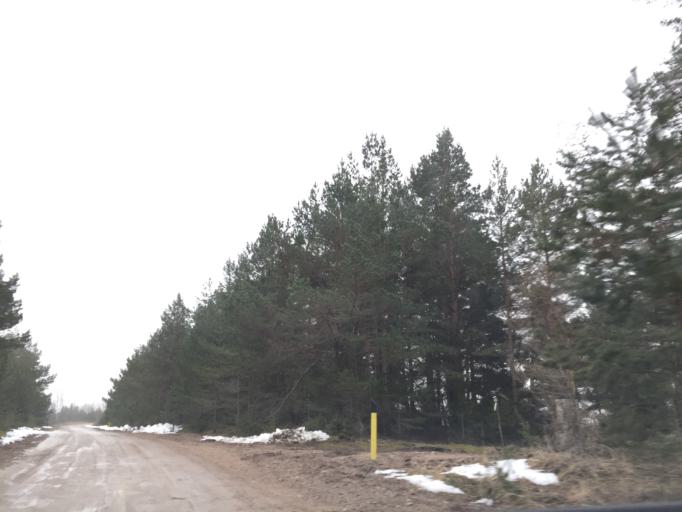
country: EE
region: Saare
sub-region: Kuressaare linn
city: Kuressaare
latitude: 58.4957
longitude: 21.9835
